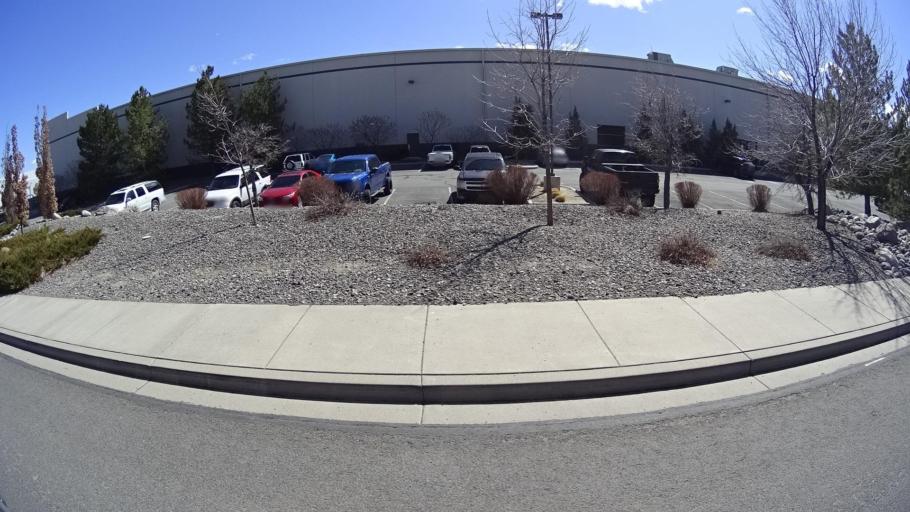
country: US
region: Nevada
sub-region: Washoe County
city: Lemmon Valley
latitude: 39.6449
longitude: -119.8623
